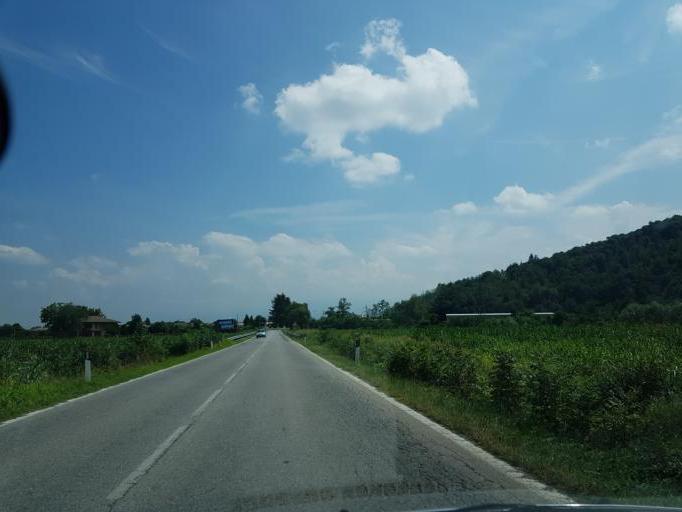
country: IT
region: Piedmont
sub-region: Provincia di Cuneo
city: Caraglio
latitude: 44.4348
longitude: 7.4196
